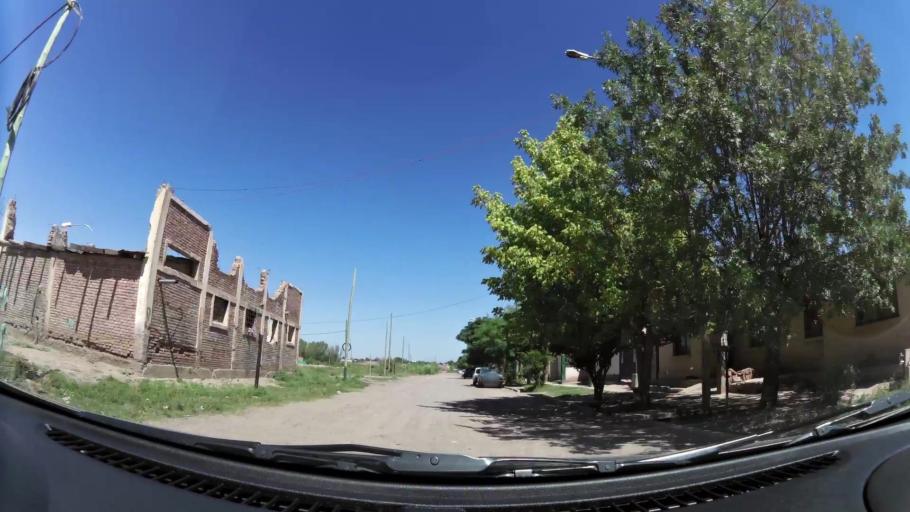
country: AR
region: Mendoza
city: Villa Nueva
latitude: -32.8723
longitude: -68.7842
